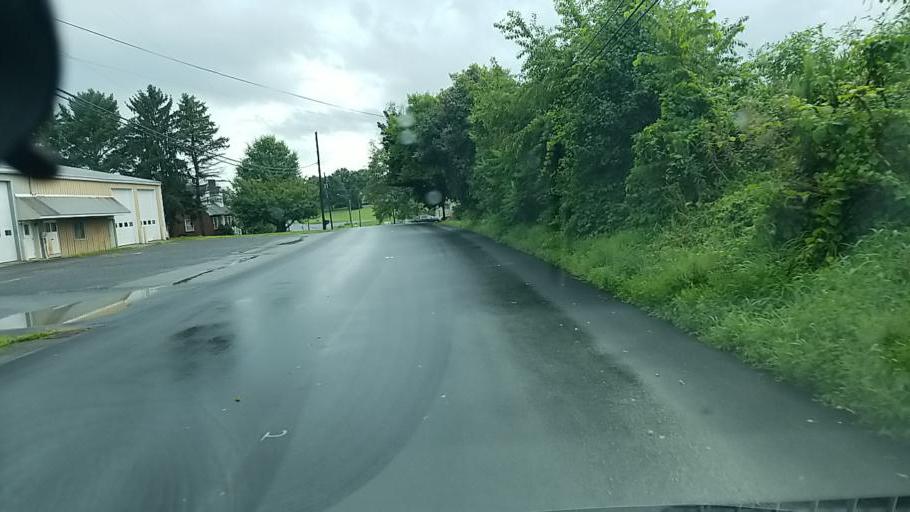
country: US
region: Pennsylvania
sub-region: Dauphin County
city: Millersburg
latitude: 40.5515
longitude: -76.9424
